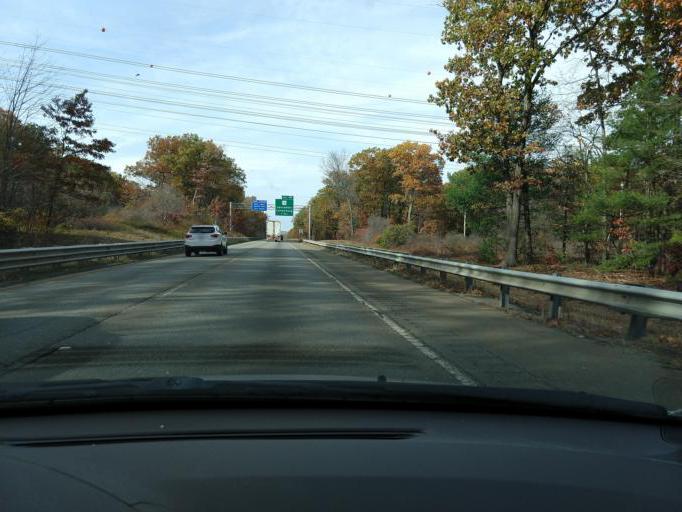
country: US
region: Massachusetts
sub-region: Middlesex County
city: Shirley
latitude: 42.5168
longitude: -71.6698
